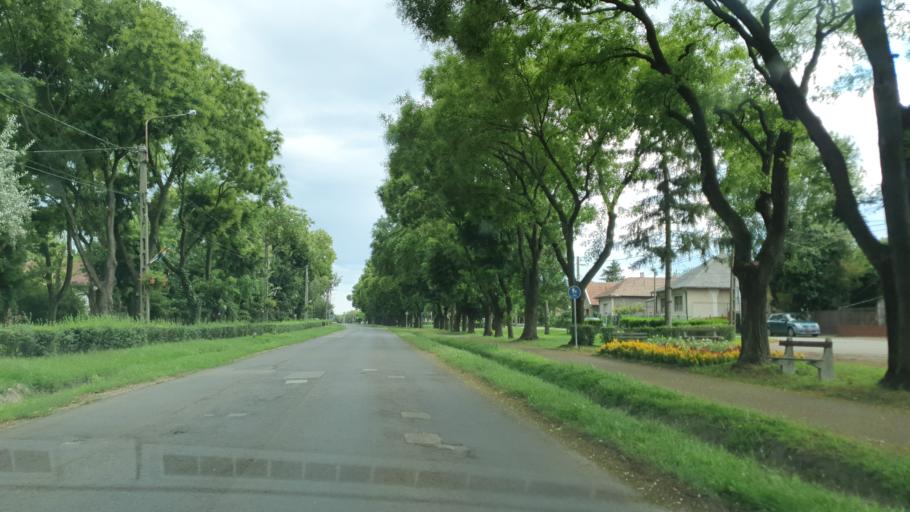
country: HU
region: Heves
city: Lorinci
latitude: 47.7418
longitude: 19.6786
